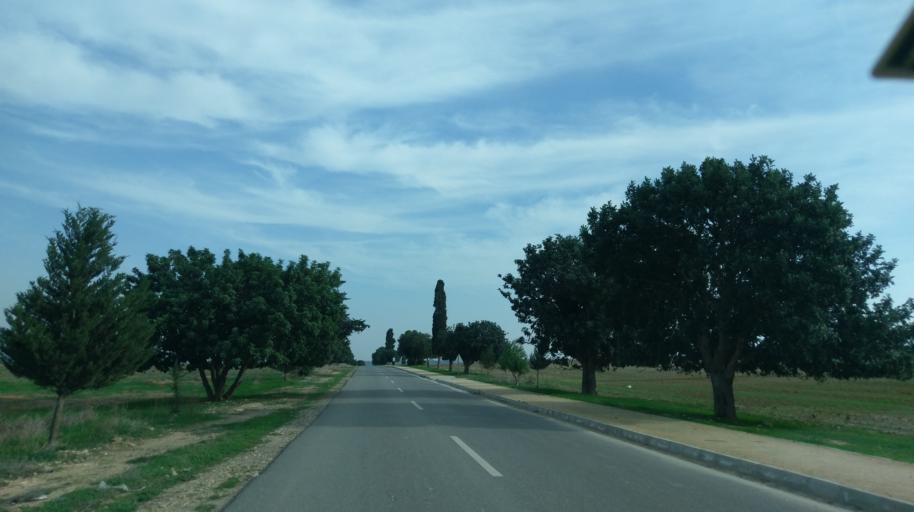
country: CY
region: Lefkosia
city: Mammari
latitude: 35.1972
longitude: 33.2361
